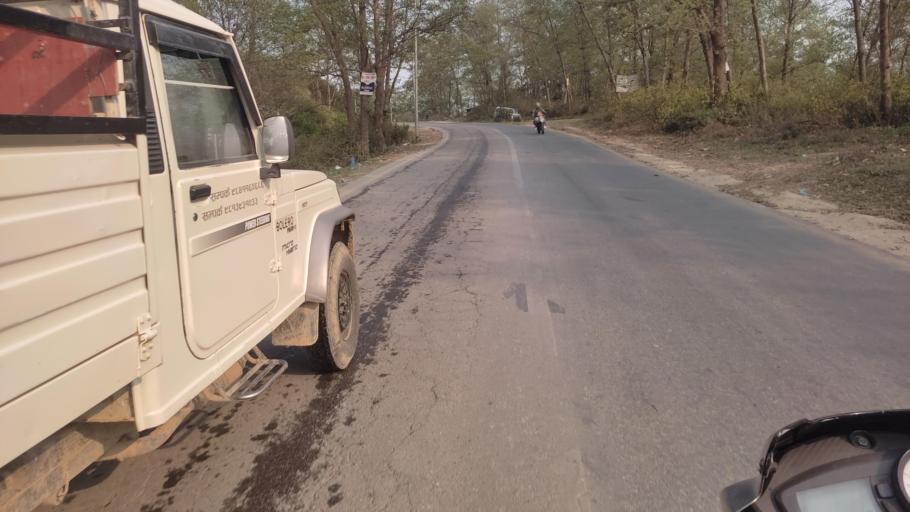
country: NP
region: Central Region
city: Kirtipur
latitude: 27.6613
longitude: 85.2902
